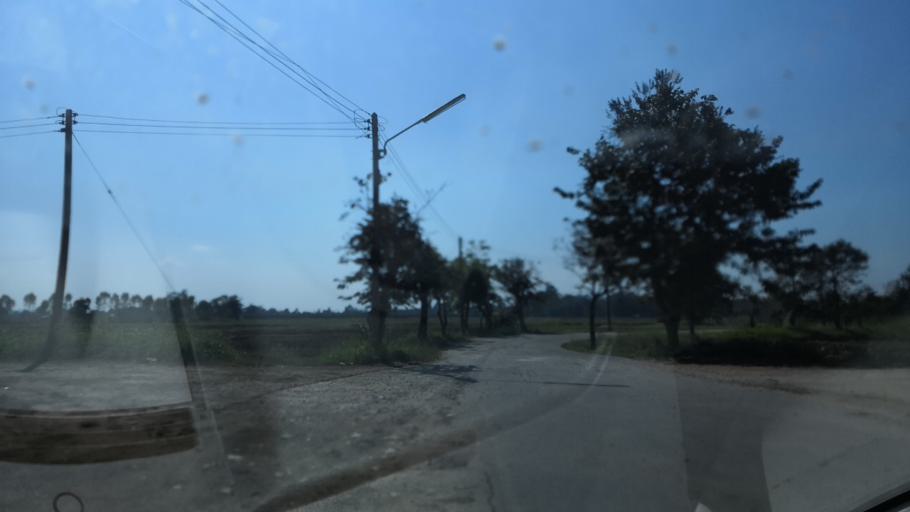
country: TH
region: Chiang Rai
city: Wiang Chai
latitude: 19.8858
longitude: 99.9464
